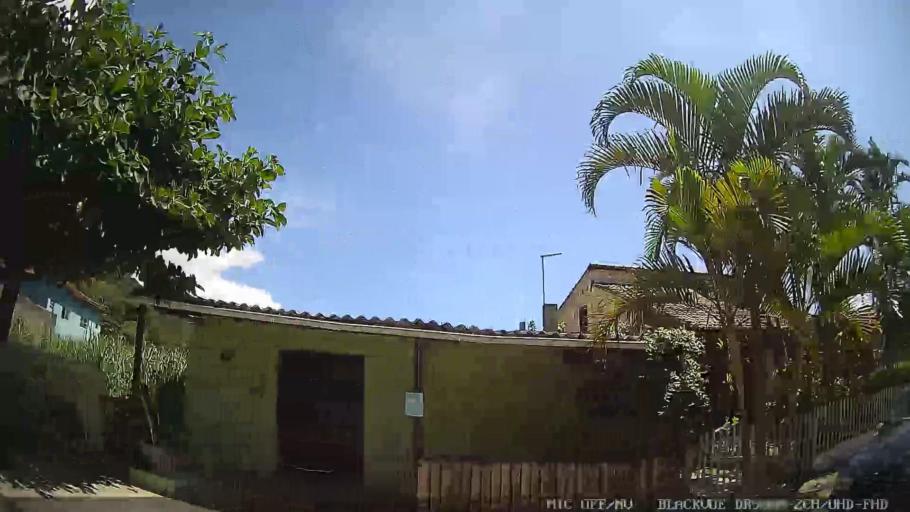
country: BR
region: Sao Paulo
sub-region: Peruibe
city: Peruibe
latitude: -24.3348
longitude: -47.0036
